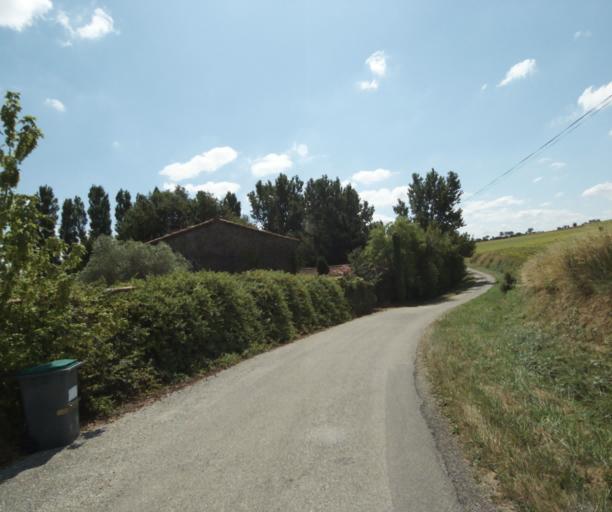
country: FR
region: Midi-Pyrenees
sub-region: Departement de la Haute-Garonne
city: Saint-Felix-Lauragais
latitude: 43.4690
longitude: 1.8390
